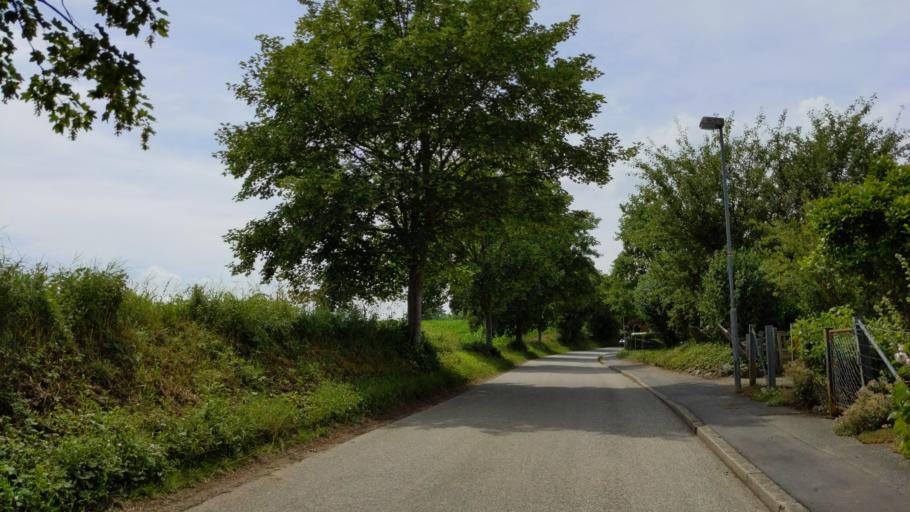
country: DE
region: Schleswig-Holstein
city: Susel
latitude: 54.1152
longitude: 10.7330
